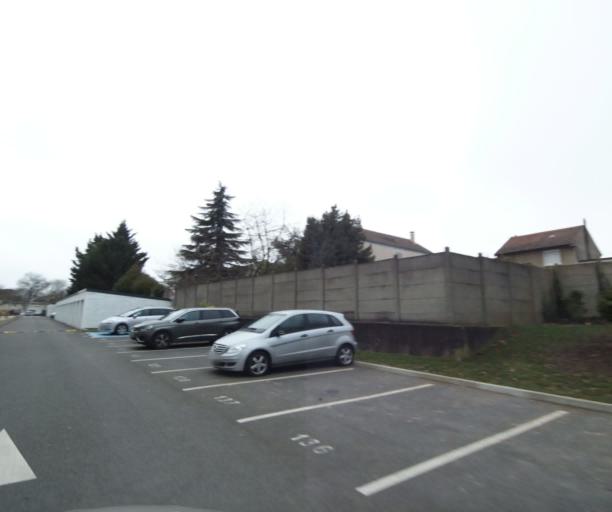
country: FR
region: Ile-de-France
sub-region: Departement du Val-de-Marne
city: Villeneuve-le-Roi
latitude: 48.7380
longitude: 2.4038
